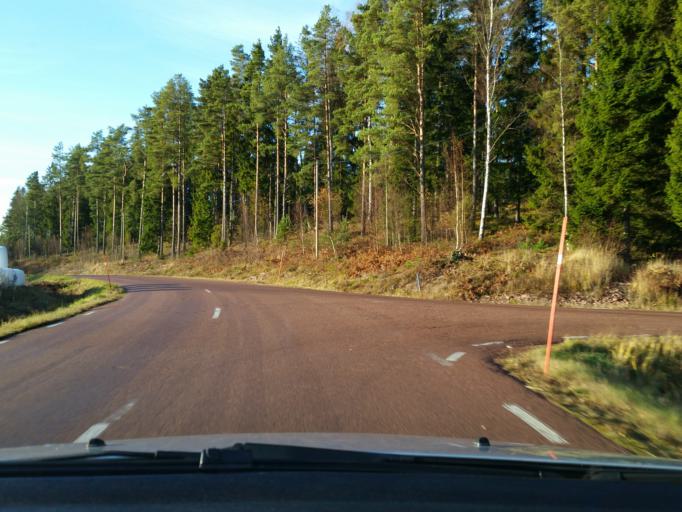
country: AX
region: Alands landsbygd
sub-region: Sund
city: Sund
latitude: 60.3091
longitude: 20.1611
